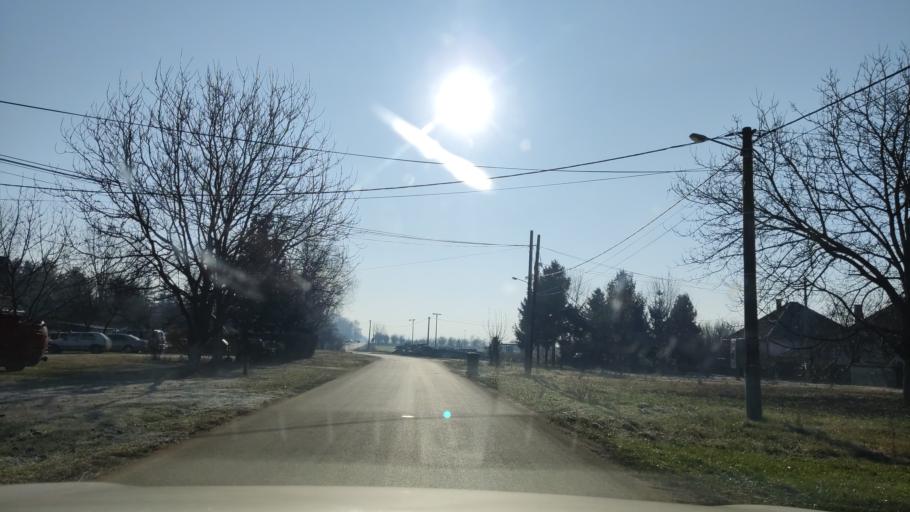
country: RS
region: Central Serbia
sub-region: Belgrade
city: Surcin
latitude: 44.7465
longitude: 20.2702
